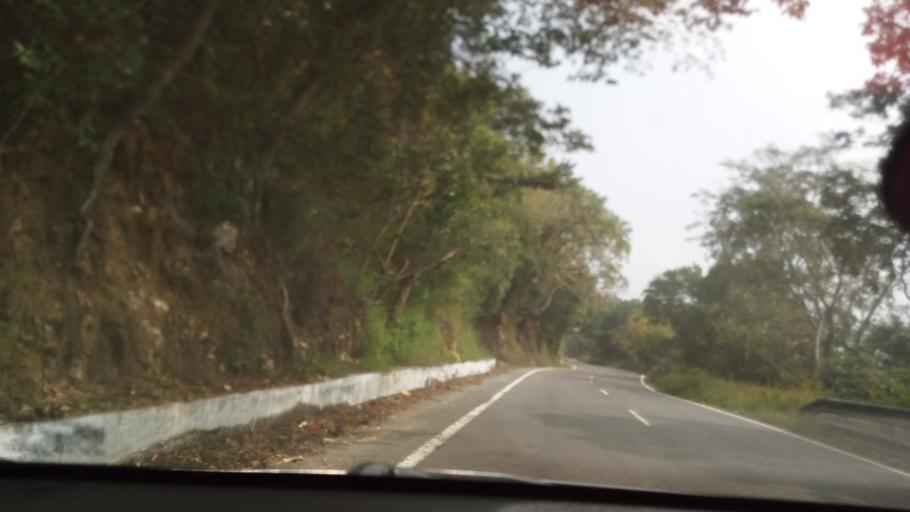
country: IN
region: Tamil Nadu
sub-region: Erode
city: Sathyamangalam
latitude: 11.6037
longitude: 77.1295
